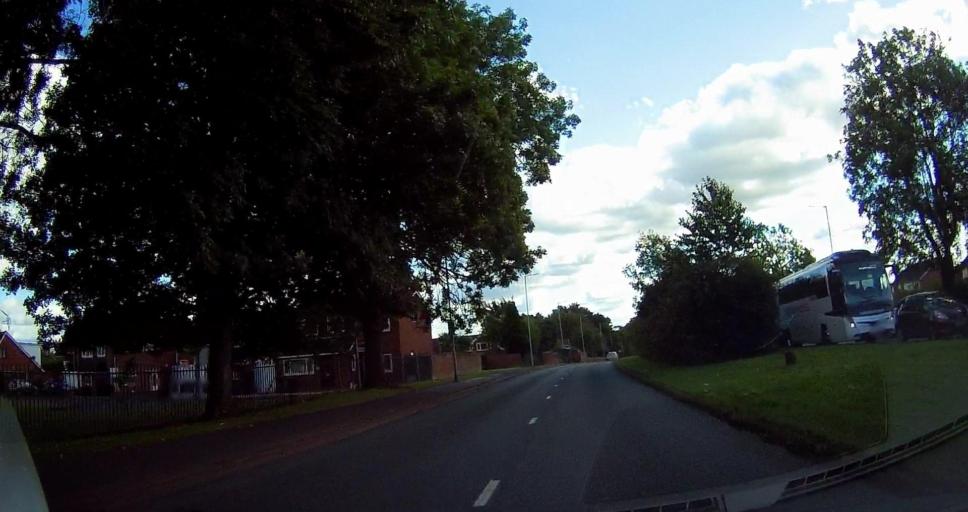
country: GB
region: England
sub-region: Staffordshire
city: Stafford
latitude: 52.8306
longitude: -2.1308
